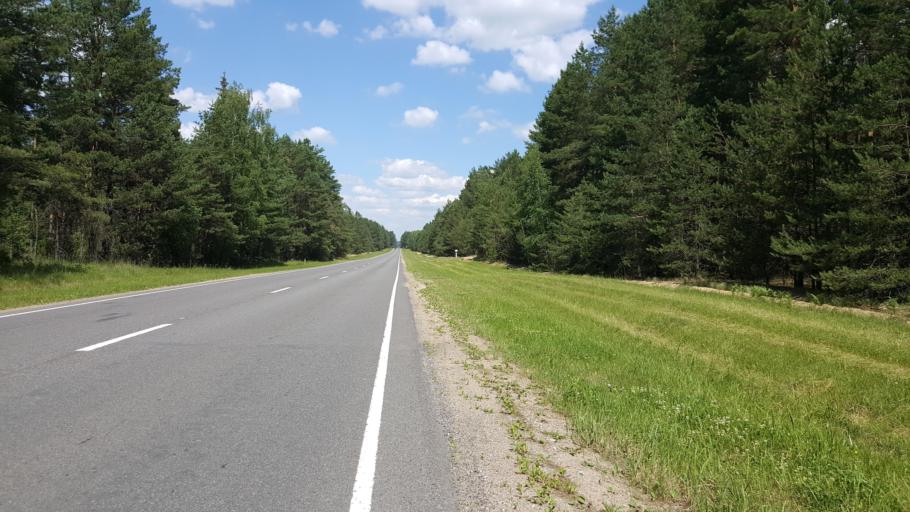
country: BY
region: Brest
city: Kamyanyuki
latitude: 52.5346
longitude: 23.7919
